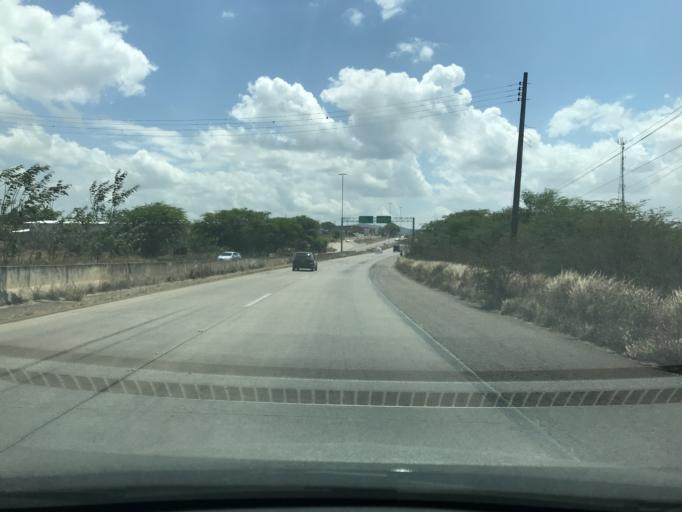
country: BR
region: Pernambuco
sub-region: Bezerros
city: Bezerros
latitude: -8.2988
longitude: -35.8395
